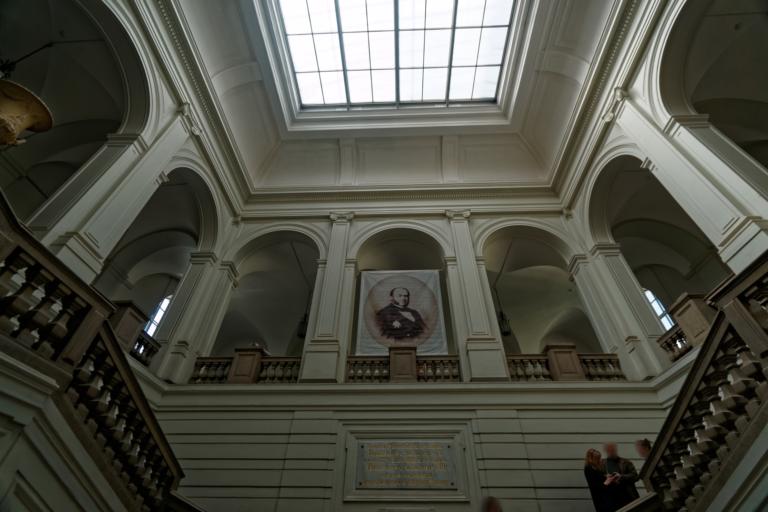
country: RU
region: St.-Petersburg
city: Centralniy
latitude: 59.9436
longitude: 30.3409
